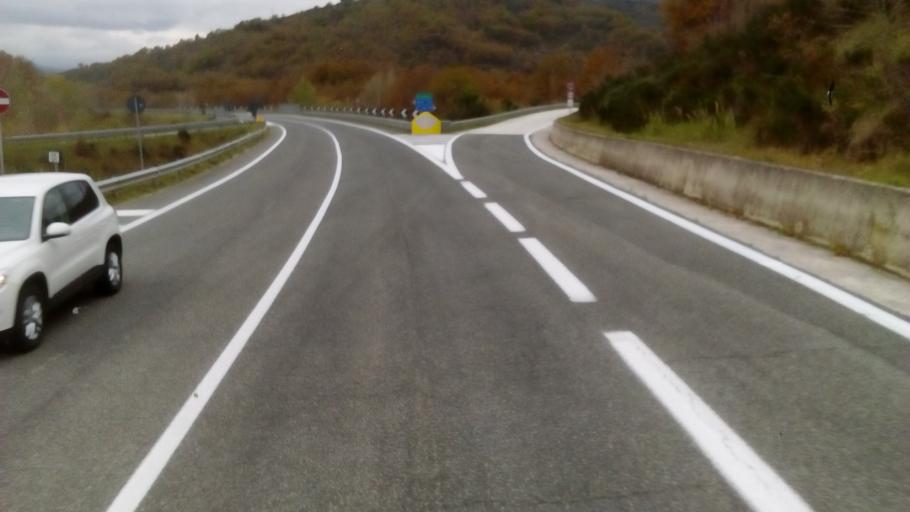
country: IT
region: Molise
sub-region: Provincia di Campobasso
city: Salcito
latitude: 41.7725
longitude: 14.4935
